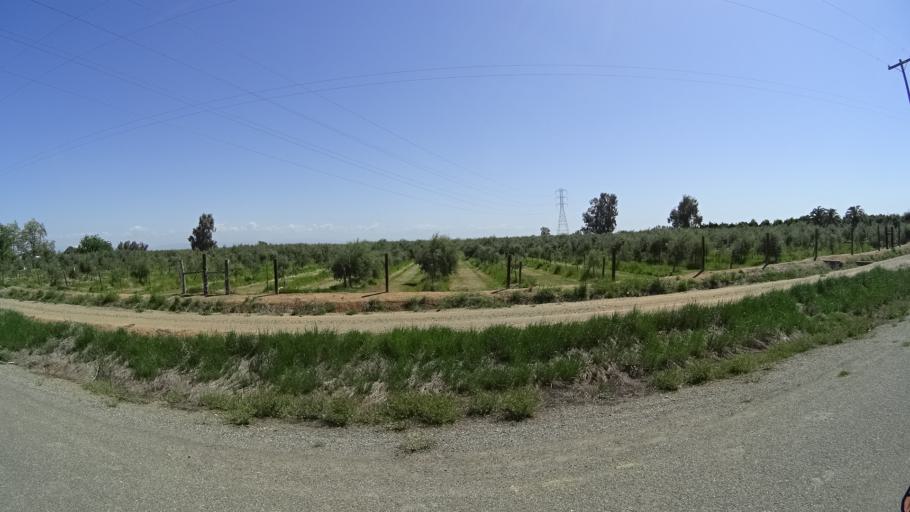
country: US
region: California
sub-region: Glenn County
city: Orland
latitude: 39.7934
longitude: -122.1692
